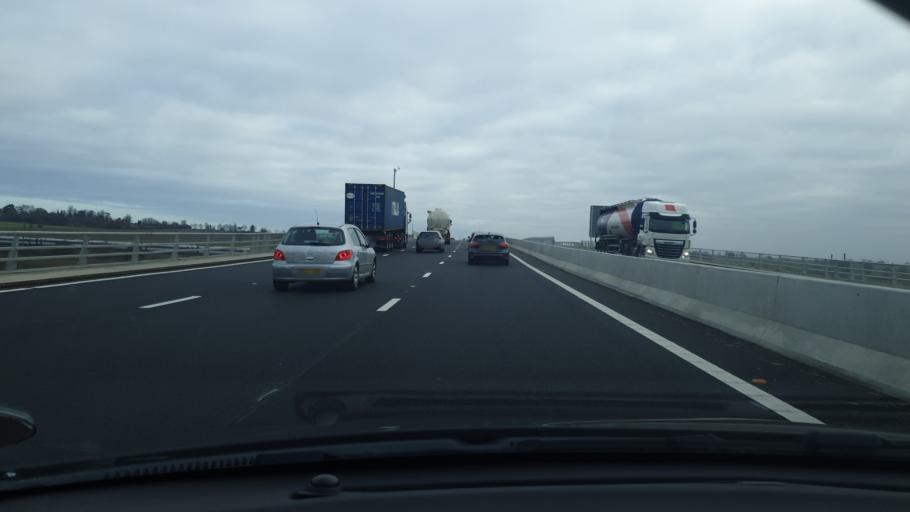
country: GB
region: England
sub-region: Cambridgeshire
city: Brampton
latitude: 52.2995
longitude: -0.2132
